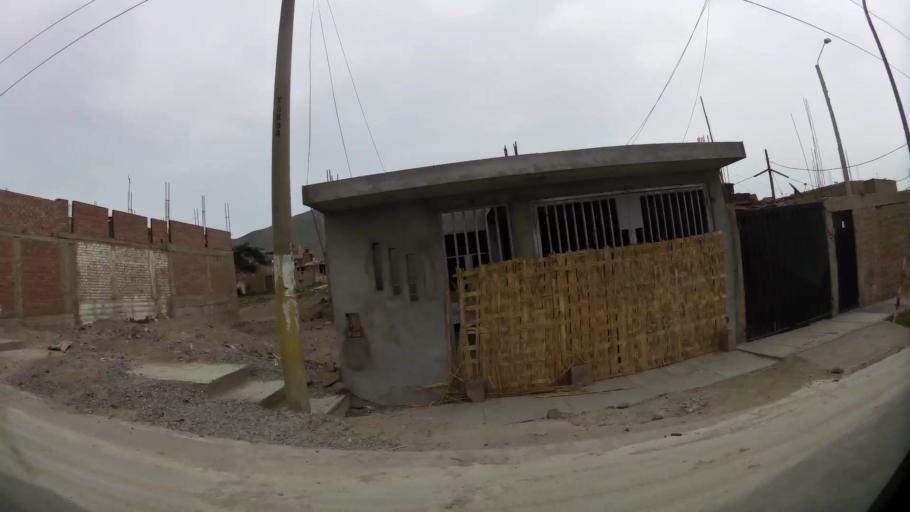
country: PE
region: Lima
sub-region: Lima
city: Santa Rosa
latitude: -11.7913
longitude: -77.1569
